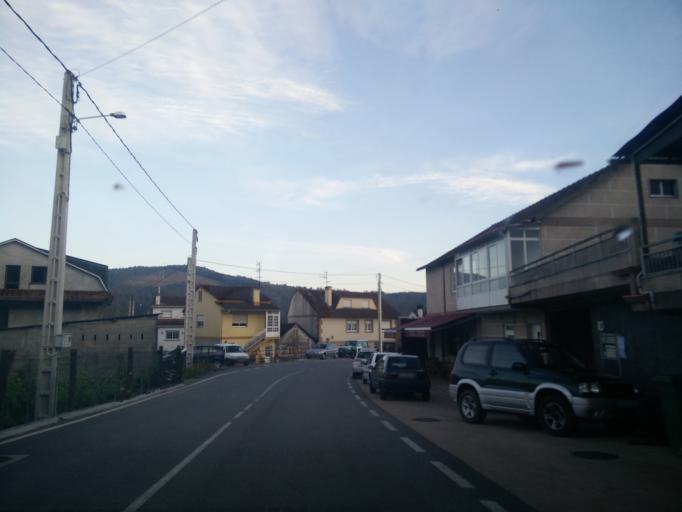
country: ES
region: Galicia
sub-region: Provincia de Pontevedra
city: Mondariz
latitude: 42.2455
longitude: -8.4413
